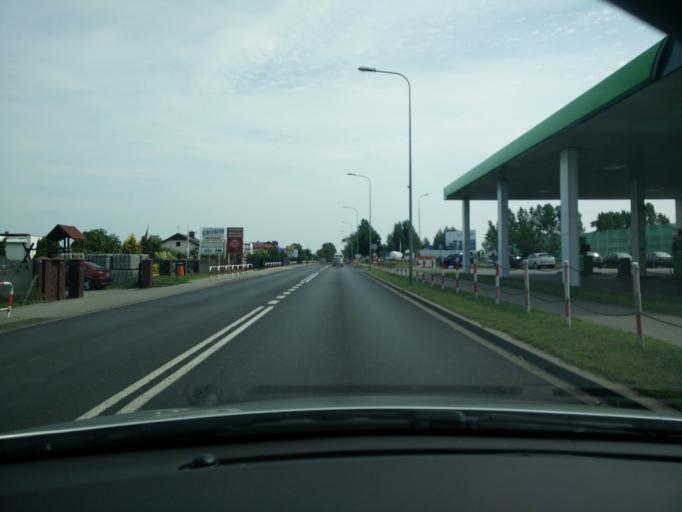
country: PL
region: Greater Poland Voivodeship
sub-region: Powiat slupecki
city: Strzalkowo
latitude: 52.3075
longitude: 17.8252
